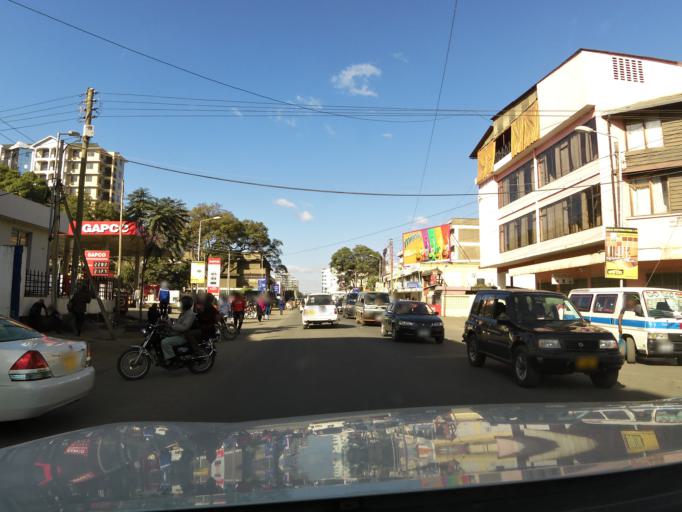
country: TZ
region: Arusha
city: Arusha
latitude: -3.3745
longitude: 36.6826
